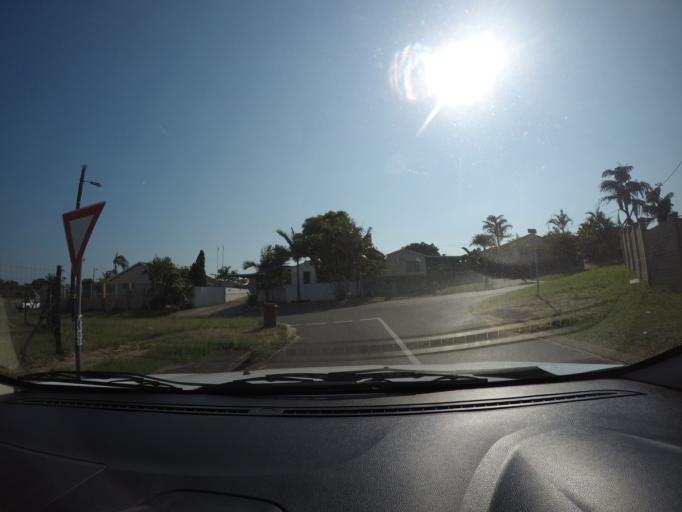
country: ZA
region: KwaZulu-Natal
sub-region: uThungulu District Municipality
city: Richards Bay
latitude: -28.7183
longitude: 32.0437
